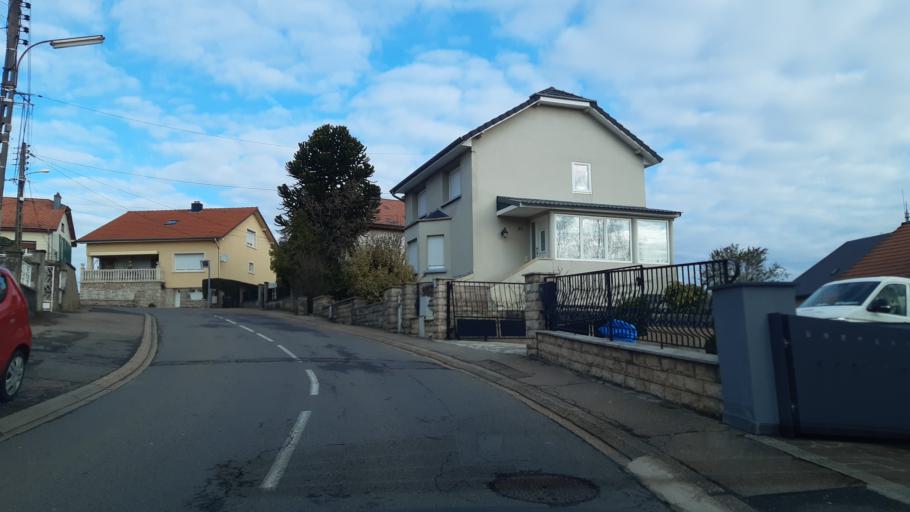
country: FR
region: Lorraine
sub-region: Departement de la Moselle
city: Audun-le-Tiche
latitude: 49.4742
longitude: 5.9494
